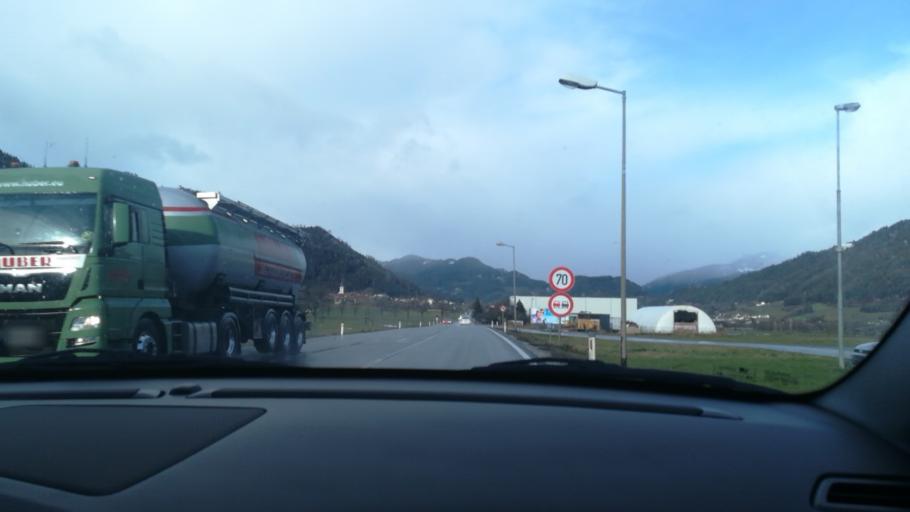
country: AT
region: Styria
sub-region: Politischer Bezirk Murtal
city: Sankt Peter ob Judenburg
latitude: 47.1778
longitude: 14.6061
